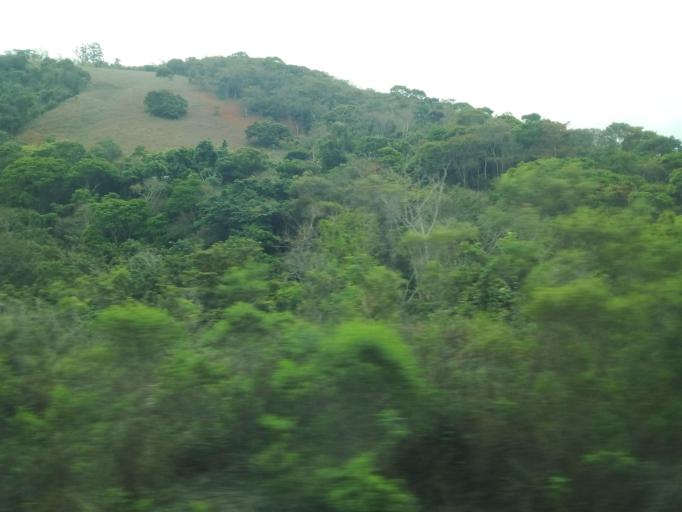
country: BR
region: Minas Gerais
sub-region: Nova Era
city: Nova Era
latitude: -19.7225
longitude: -42.9684
